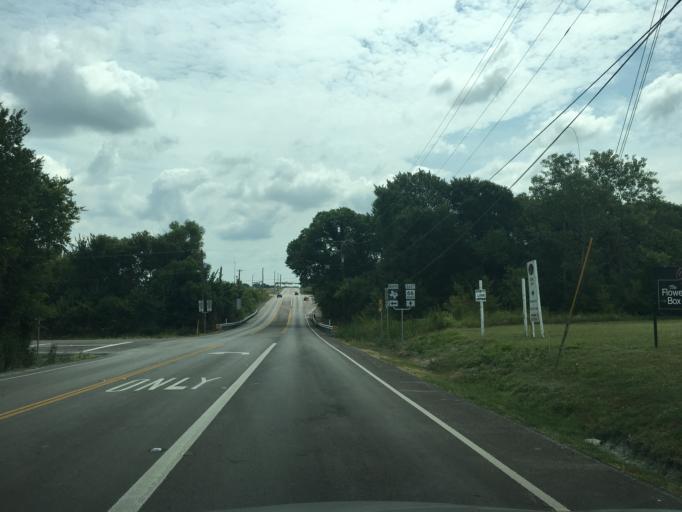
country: US
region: Texas
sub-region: Rockwall County
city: Rockwall
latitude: 32.9364
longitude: -96.4441
